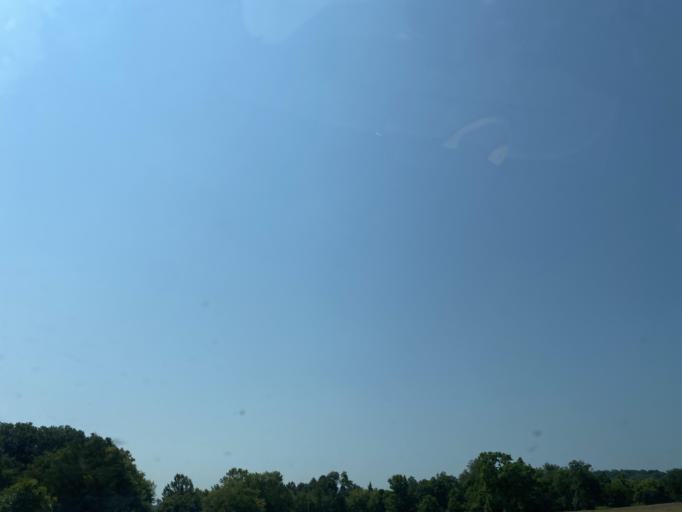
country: US
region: Kentucky
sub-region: Campbell County
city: Claryville
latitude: 38.8358
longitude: -84.4578
